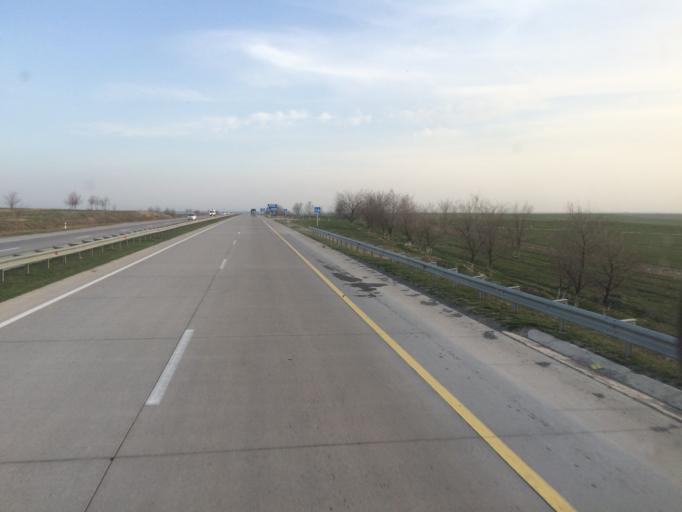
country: KZ
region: Ongtustik Qazaqstan
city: Temirlanovka
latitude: 42.6597
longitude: 69.2321
